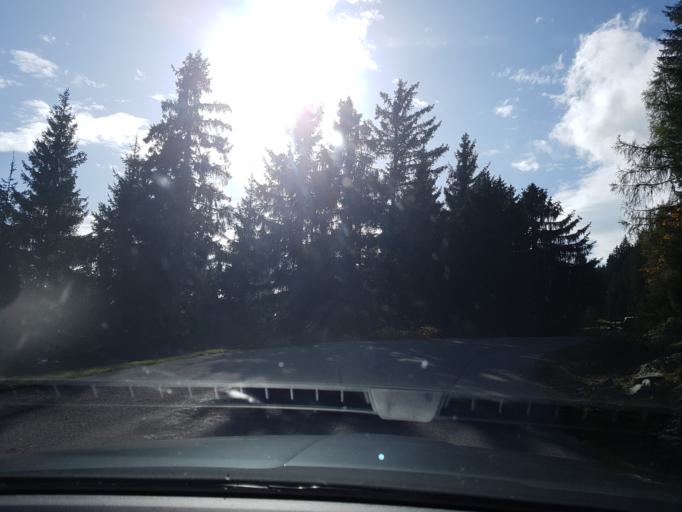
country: AT
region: Salzburg
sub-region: Politischer Bezirk Sankt Johann im Pongau
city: Filzmoos
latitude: 47.4089
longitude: 13.4978
